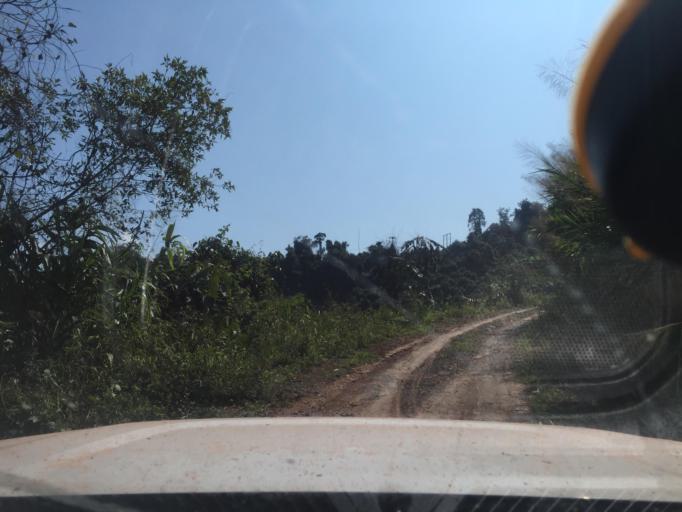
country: LA
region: Phongsali
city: Phongsali
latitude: 21.6555
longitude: 102.4149
